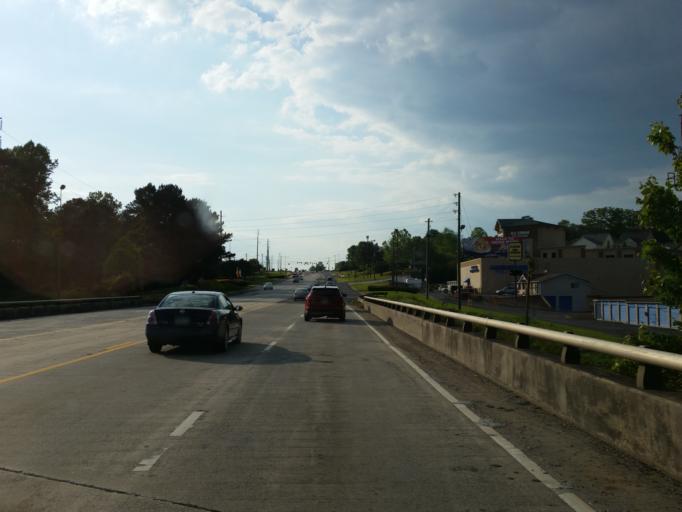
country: US
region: Georgia
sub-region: Cobb County
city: Vinings
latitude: 33.8399
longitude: -84.4959
